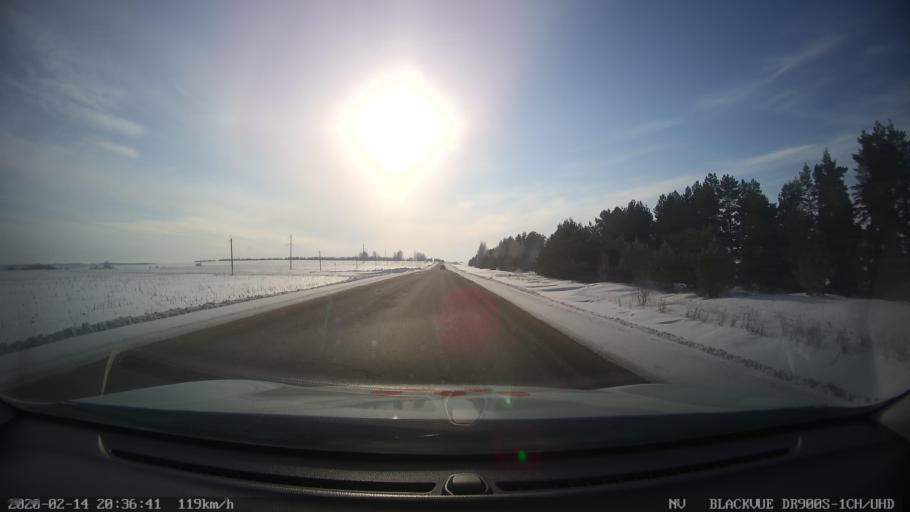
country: RU
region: Tatarstan
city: Kuybyshevskiy Zaton
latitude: 55.3631
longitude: 49.0018
